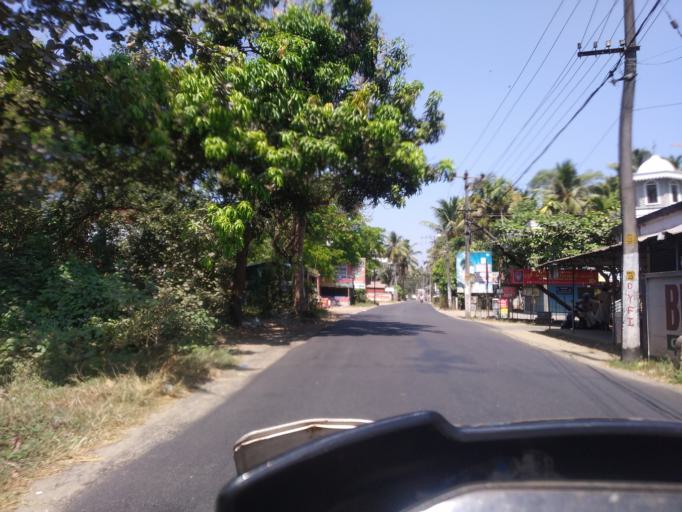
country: IN
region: Kerala
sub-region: Thrissur District
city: Kodungallur
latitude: 10.1653
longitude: 76.2134
